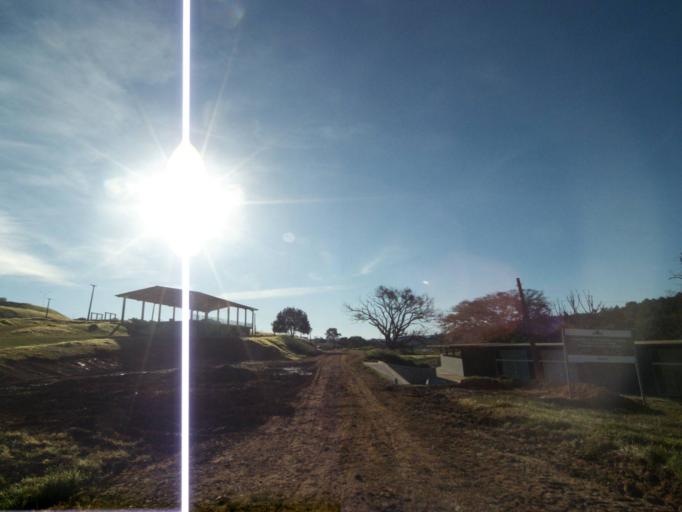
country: BR
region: Parana
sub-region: Tibagi
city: Tibagi
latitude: -24.5277
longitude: -50.3973
